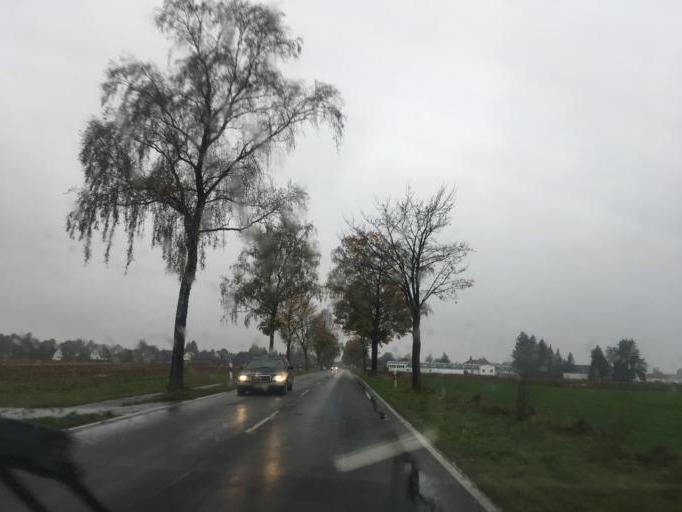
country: DE
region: Lower Saxony
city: Bergen
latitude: 52.8128
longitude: 9.9934
